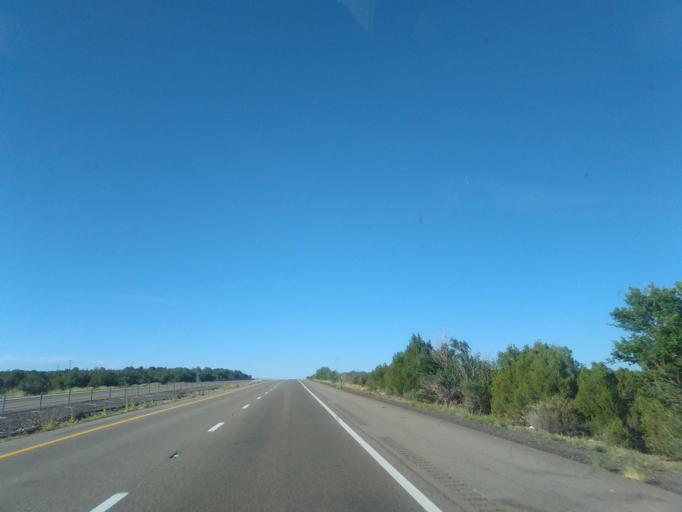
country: US
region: New Mexico
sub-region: San Miguel County
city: Las Vegas
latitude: 35.4091
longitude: -105.3108
